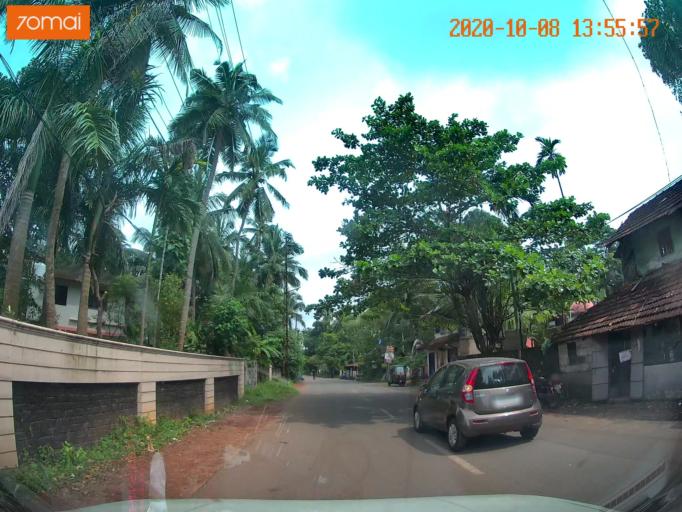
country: IN
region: Kerala
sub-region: Kozhikode
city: Kozhikode
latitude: 11.2927
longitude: 75.7968
